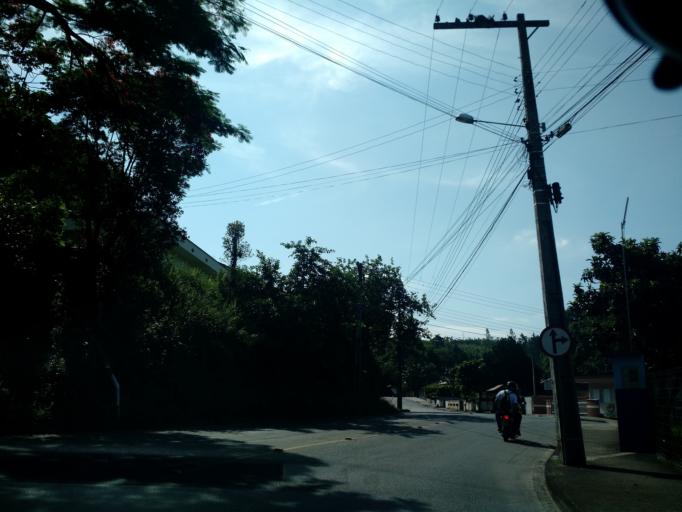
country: BR
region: Santa Catarina
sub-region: Jaragua Do Sul
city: Jaragua do Sul
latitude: -26.4967
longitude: -49.1015
